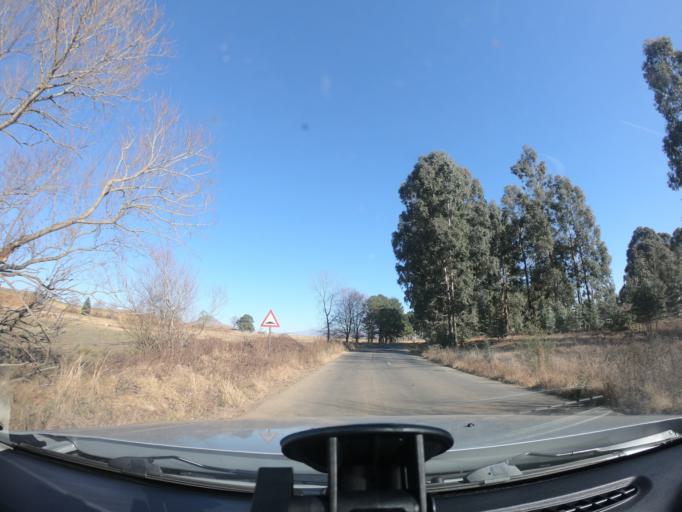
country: ZA
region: KwaZulu-Natal
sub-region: uMgungundlovu District Municipality
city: Mooirivier
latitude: -29.3293
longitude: 29.8461
